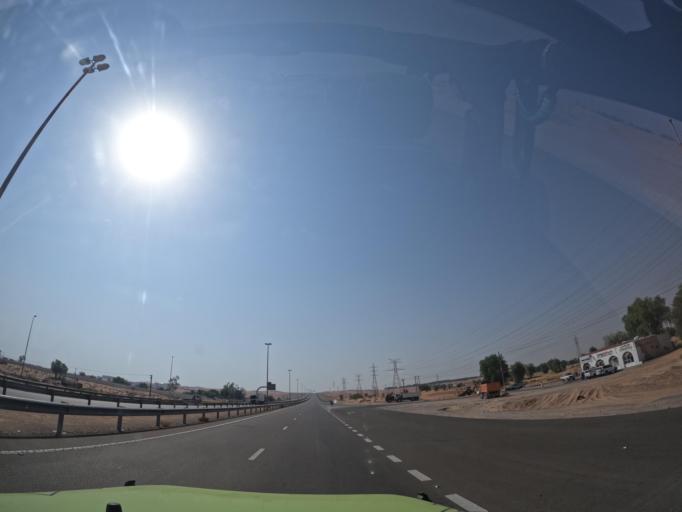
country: OM
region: Al Buraimi
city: Al Buraymi
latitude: 24.3601
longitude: 55.7319
